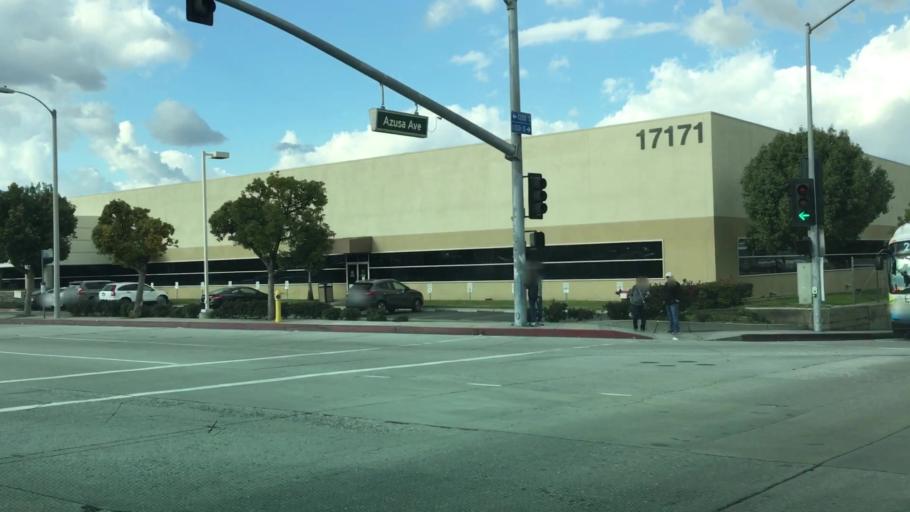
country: US
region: California
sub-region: Los Angeles County
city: La Puente
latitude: 34.0002
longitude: -117.9309
